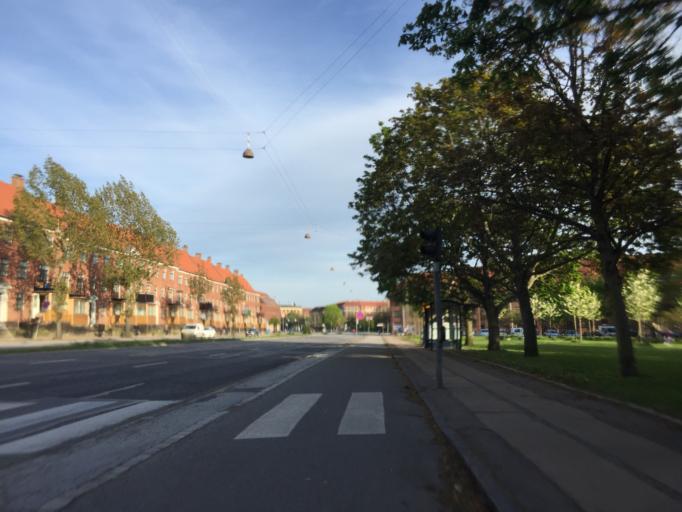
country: DK
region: Capital Region
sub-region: Frederiksberg Kommune
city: Frederiksberg
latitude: 55.6983
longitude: 12.5235
